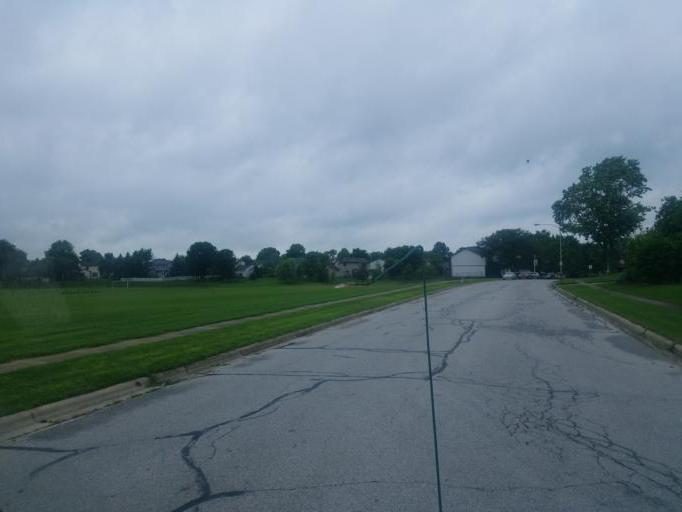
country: US
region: Ohio
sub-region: Franklin County
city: Gahanna
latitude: 40.0110
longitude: -82.8514
